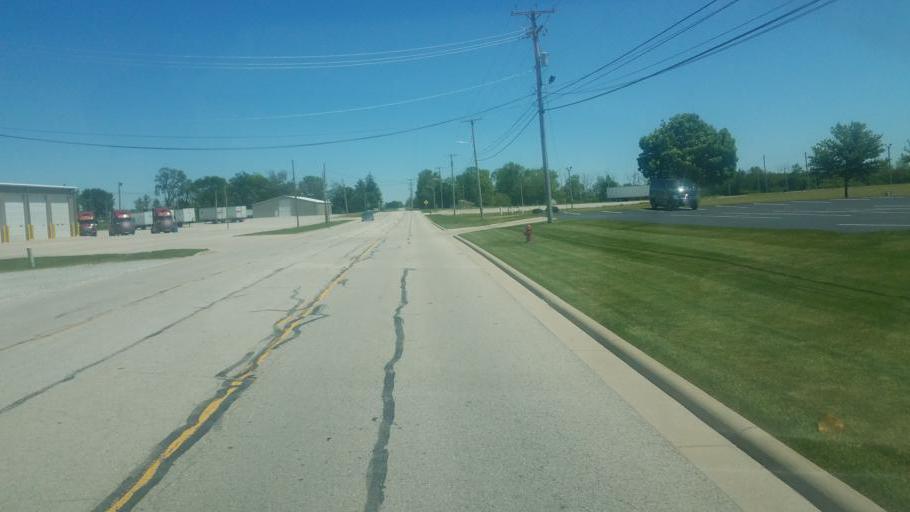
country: US
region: Ohio
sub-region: Darke County
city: Versailles
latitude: 40.2260
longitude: -84.4596
